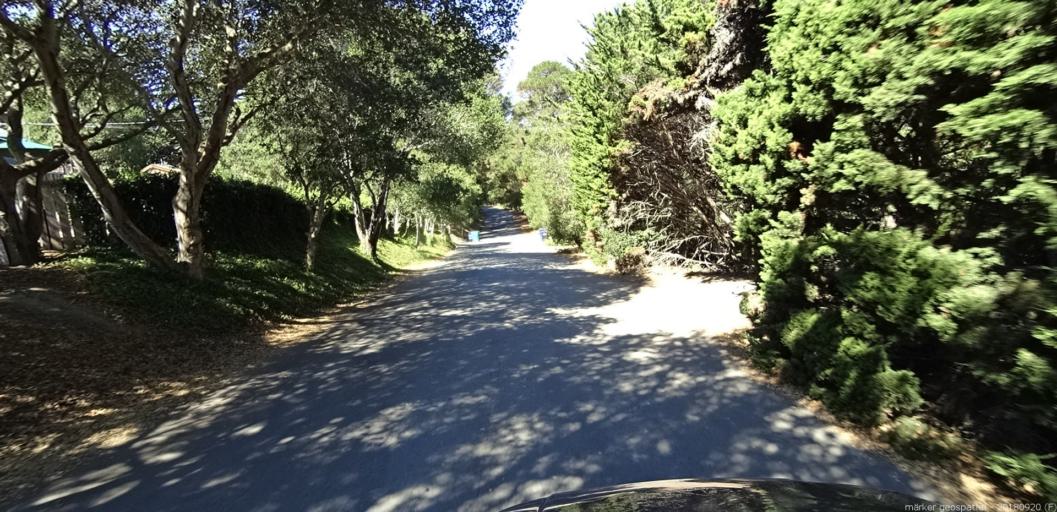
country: US
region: California
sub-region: Monterey County
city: Carmel-by-the-Sea
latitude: 36.5493
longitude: -121.9006
